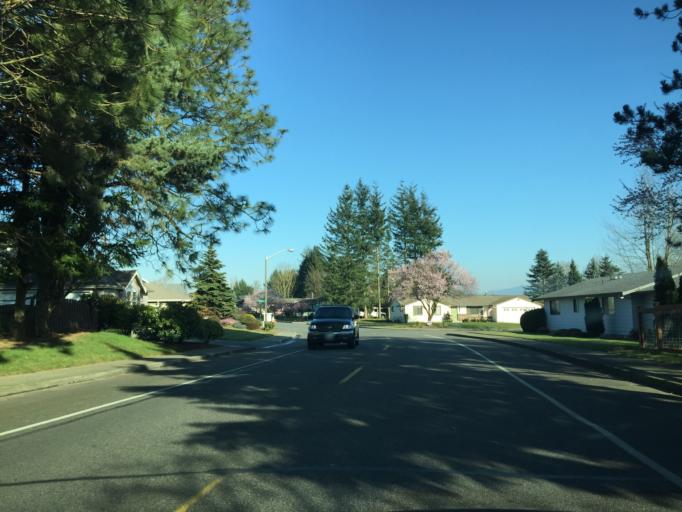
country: US
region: Washington
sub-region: Whatcom County
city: Lynden
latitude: 48.9548
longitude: -122.4408
